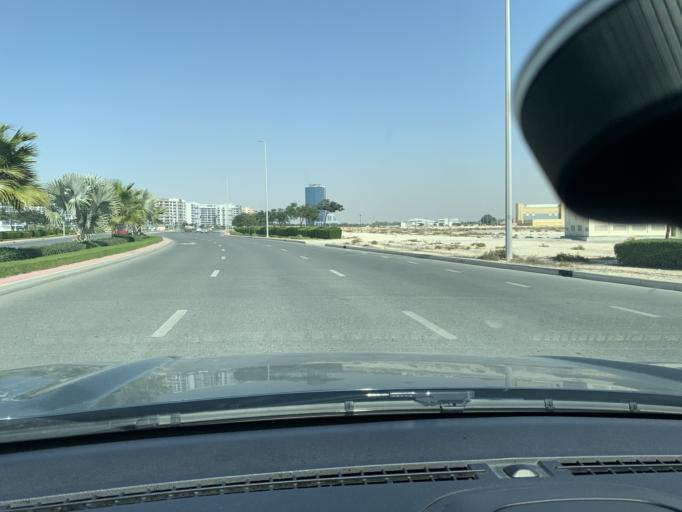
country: AE
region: Dubai
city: Dubai
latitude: 25.0358
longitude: 55.2436
